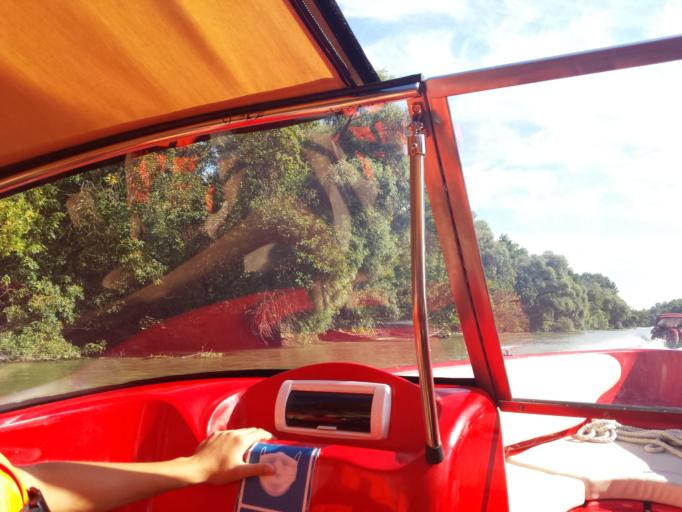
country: RO
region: Tulcea
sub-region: Comuna Nufaru
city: Nufaru
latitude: 45.2191
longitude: 28.8762
